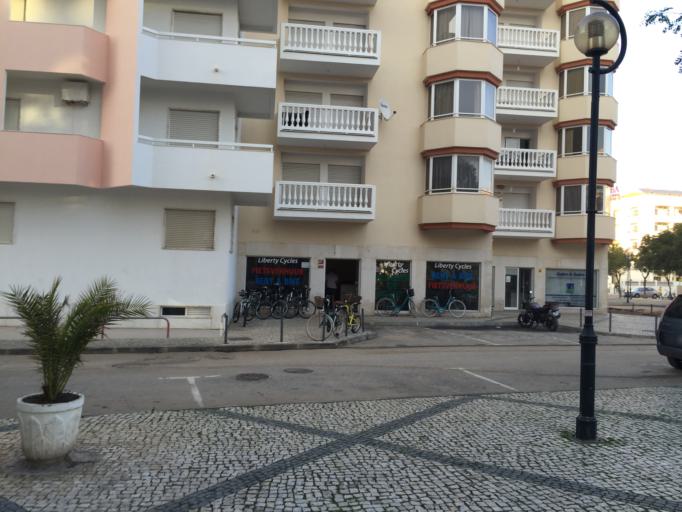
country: PT
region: Faro
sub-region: Vila Real de Santo Antonio
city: Monte Gordo
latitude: 37.1813
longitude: -7.4493
